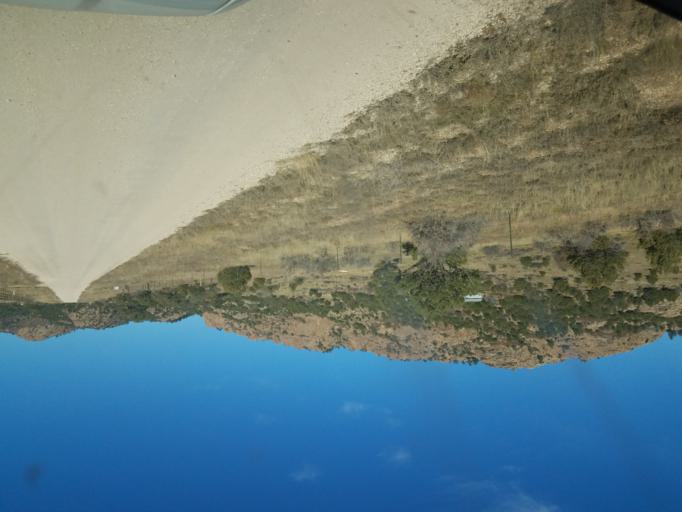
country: US
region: Colorado
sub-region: Custer County
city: Westcliffe
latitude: 38.2336
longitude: -105.4667
